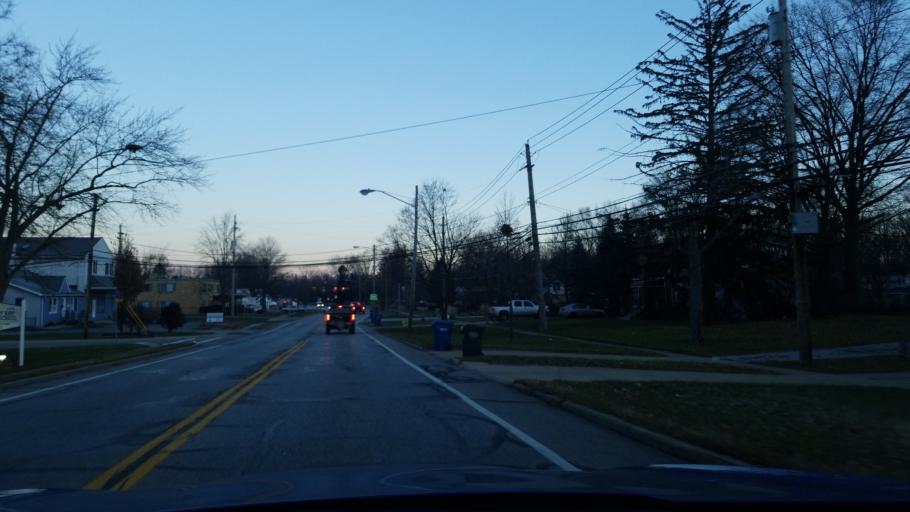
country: US
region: Ohio
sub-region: Cuyahoga County
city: Berea
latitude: 41.3487
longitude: -81.8576
